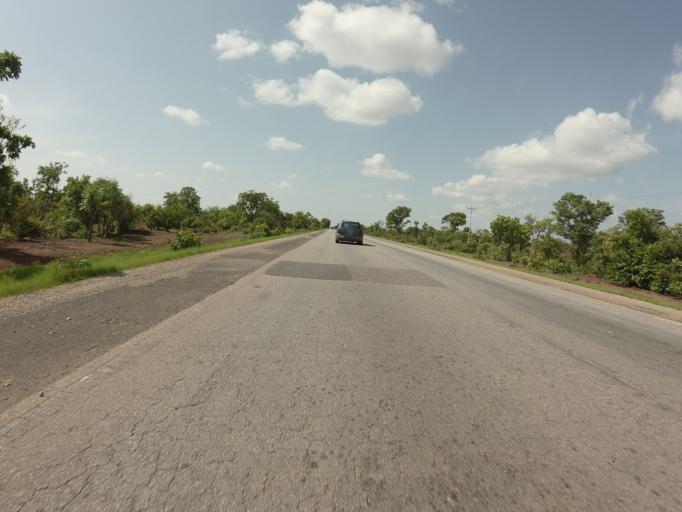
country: GH
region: Northern
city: Savelugu
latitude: 9.9552
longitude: -0.8348
